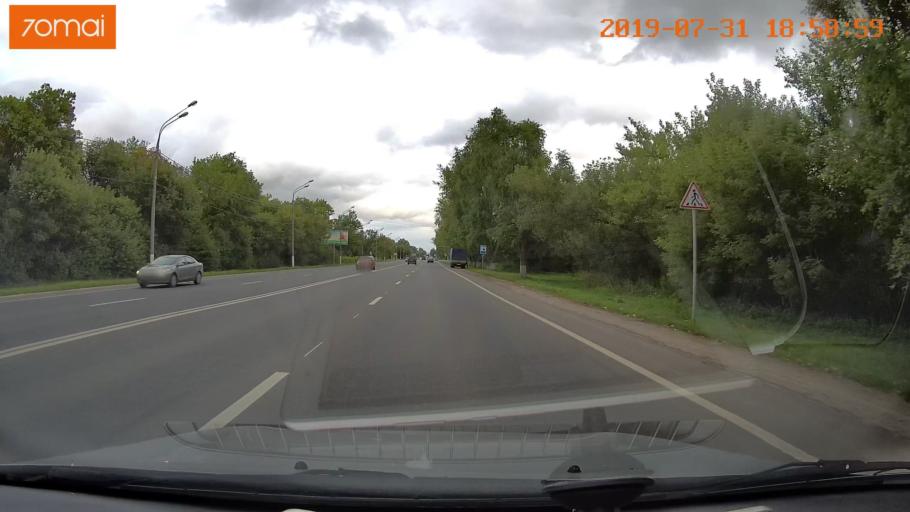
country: RU
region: Moskovskaya
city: Raduzhnyy
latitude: 55.1424
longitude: 38.7109
